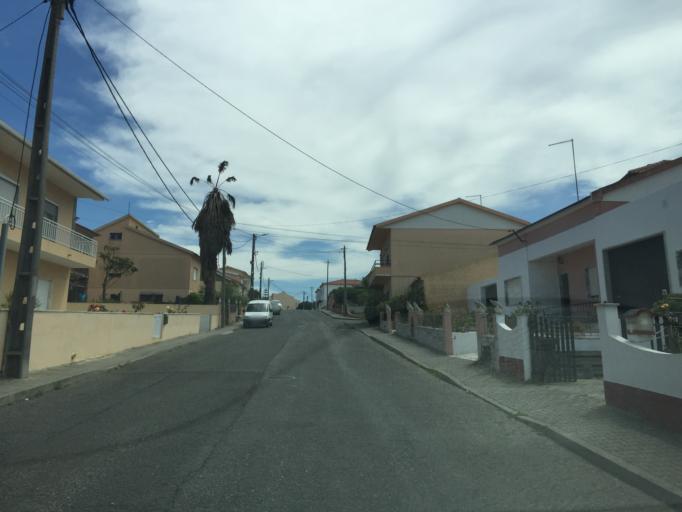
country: PT
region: Lisbon
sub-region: Lourinha
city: Lourinha
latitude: 39.2038
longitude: -9.3347
